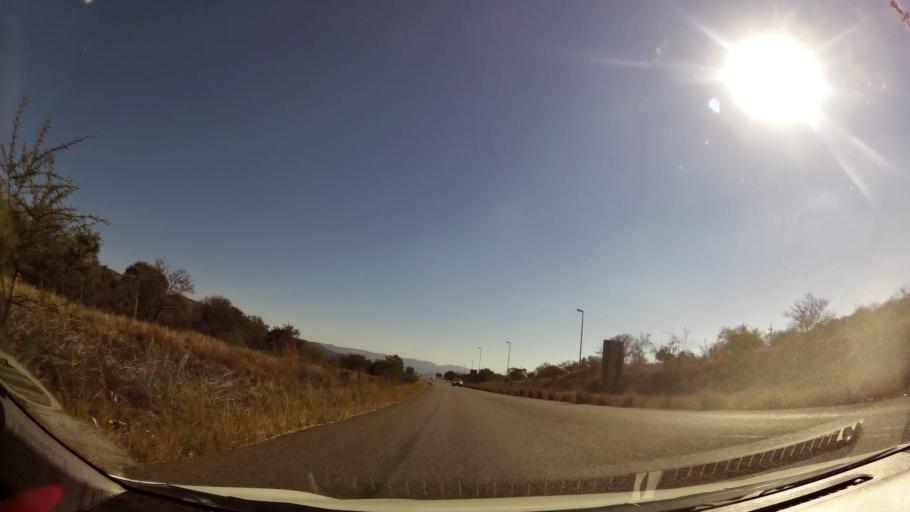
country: ZA
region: Limpopo
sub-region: Waterberg District Municipality
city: Mokopane
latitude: -24.1668
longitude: 29.0829
